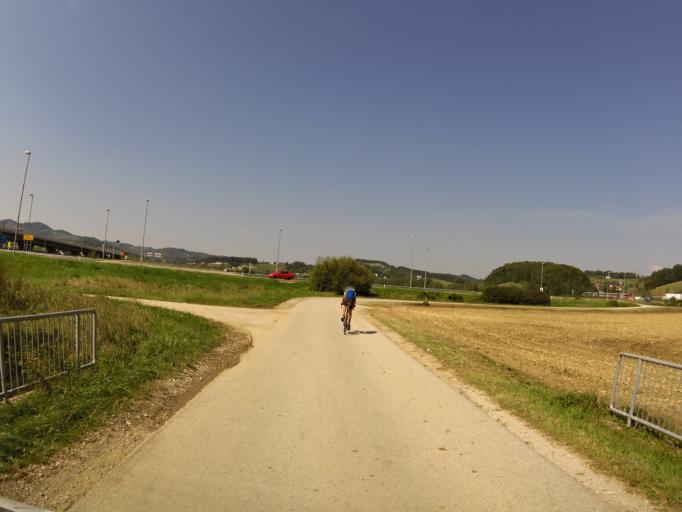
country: SI
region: Pesnica
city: Pesnica pri Mariboru
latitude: 46.5967
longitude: 15.6718
